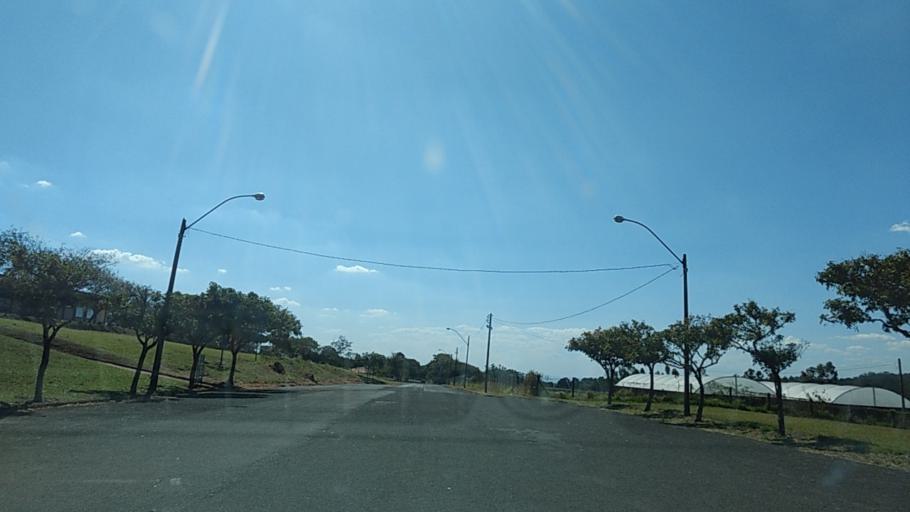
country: BR
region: Sao Paulo
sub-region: Botucatu
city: Botucatu
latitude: -22.8478
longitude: -48.4324
